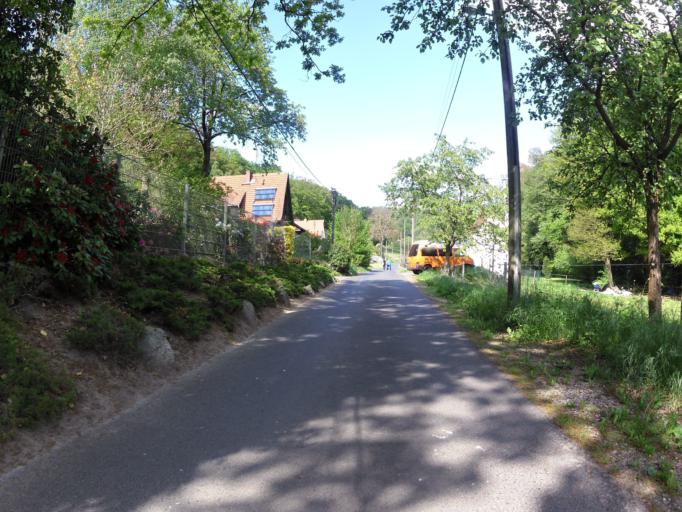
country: DE
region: Thuringia
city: Seebach
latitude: 50.9576
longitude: 10.4155
